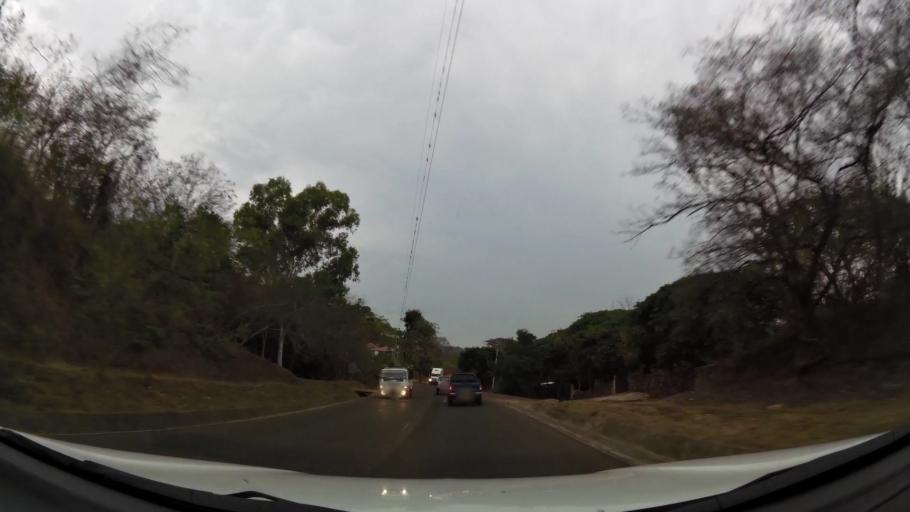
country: NI
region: Esteli
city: Esteli
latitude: 12.9976
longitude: -86.3008
